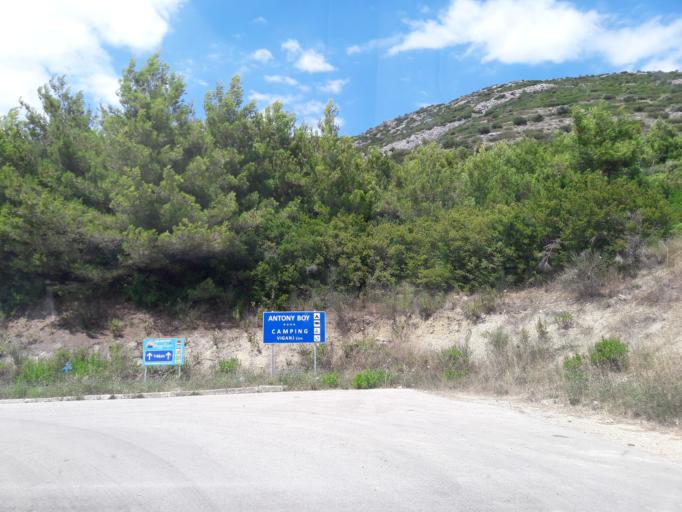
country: HR
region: Dubrovacko-Neretvanska
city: Korcula
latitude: 42.9810
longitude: 17.1224
